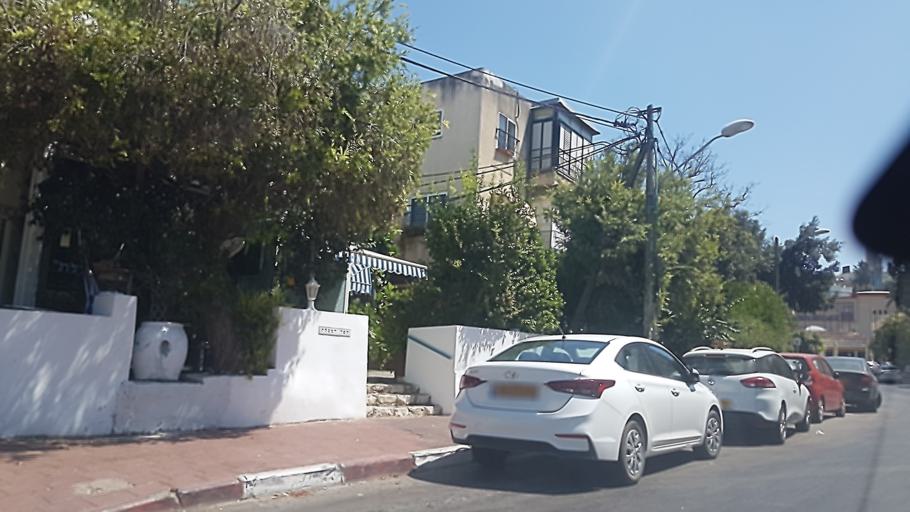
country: IL
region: Tel Aviv
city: Ramat Gan
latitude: 32.0802
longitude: 34.8220
